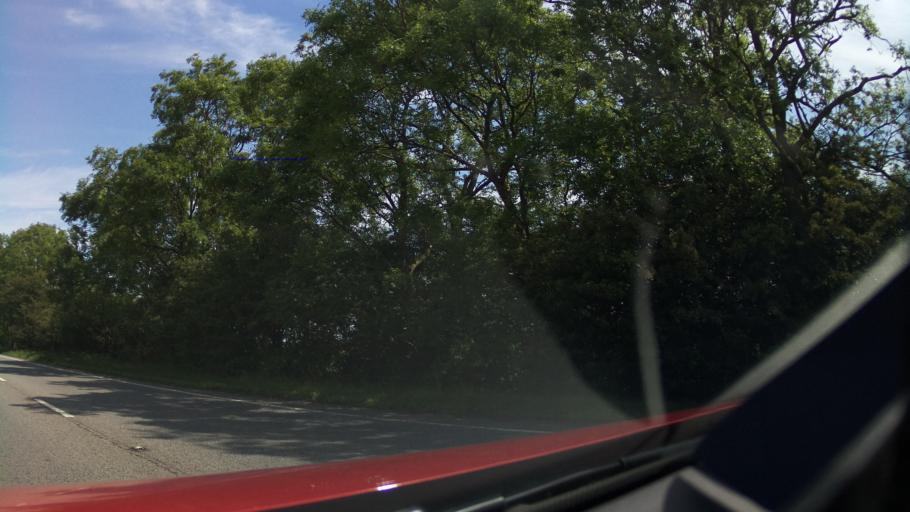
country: GB
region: England
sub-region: Lincolnshire
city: Burton
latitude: 53.3450
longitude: -0.5444
